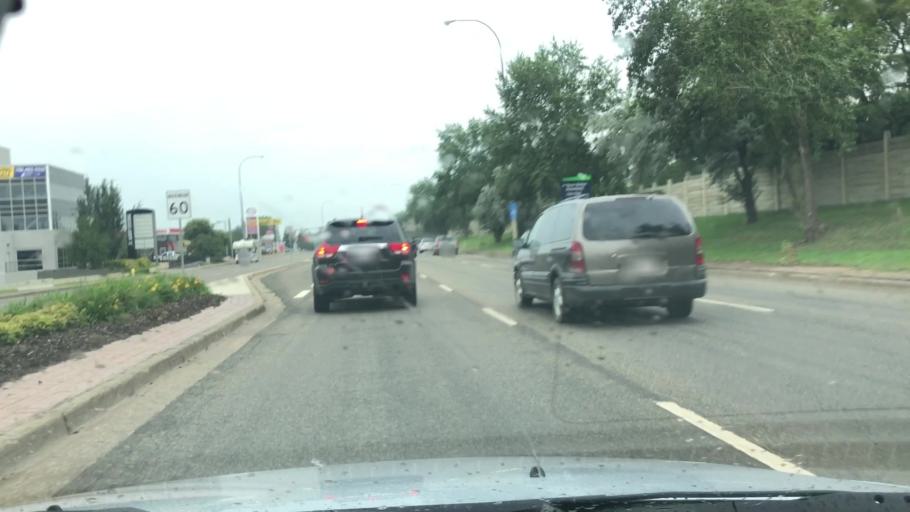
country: CA
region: Alberta
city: St. Albert
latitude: 53.6258
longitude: -113.6162
